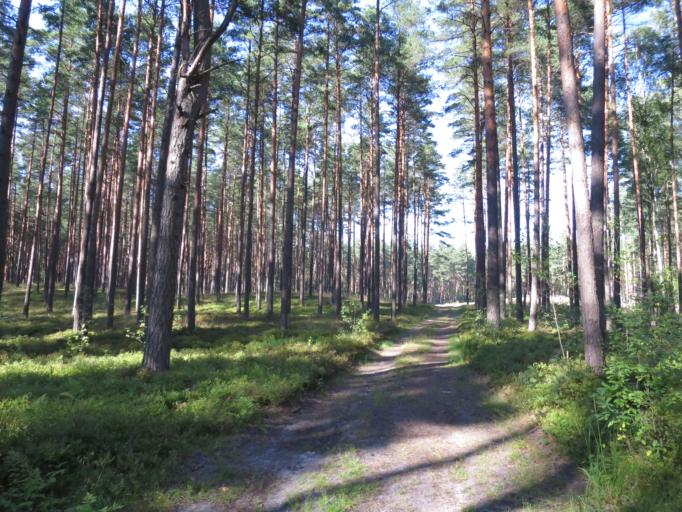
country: LV
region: Riga
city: Jaunciems
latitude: 57.0717
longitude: 24.1994
